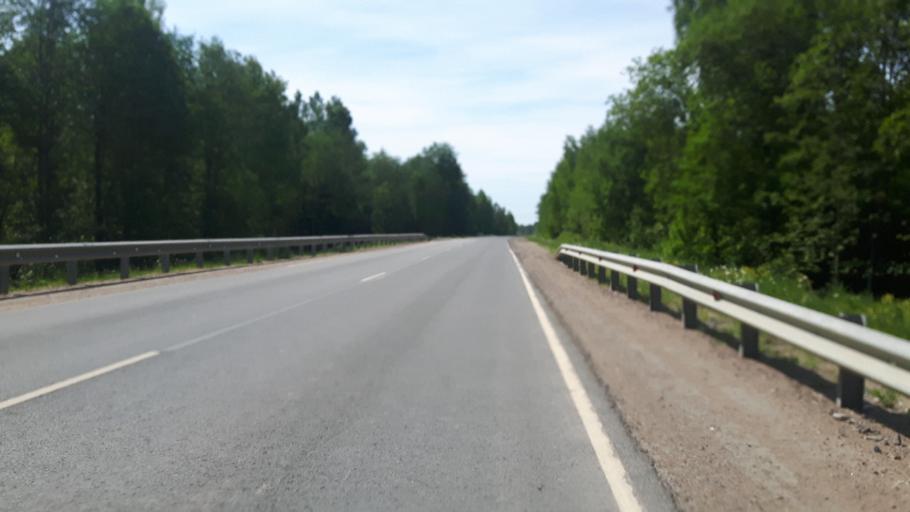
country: RU
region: Leningrad
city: Vistino
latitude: 59.6806
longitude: 28.4562
